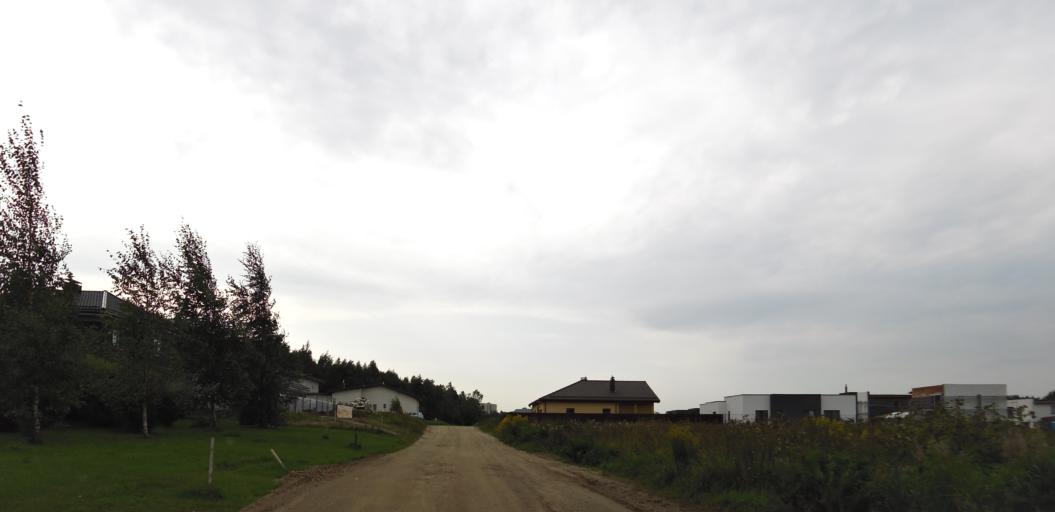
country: LT
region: Vilnius County
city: Pasilaiciai
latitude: 54.7544
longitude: 25.2296
